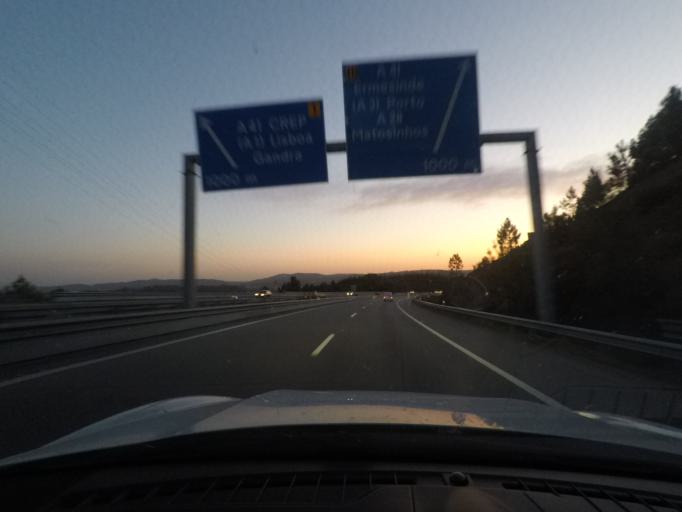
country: PT
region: Porto
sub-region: Pacos de Ferreira
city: Seroa
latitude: 41.2368
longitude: -8.4380
